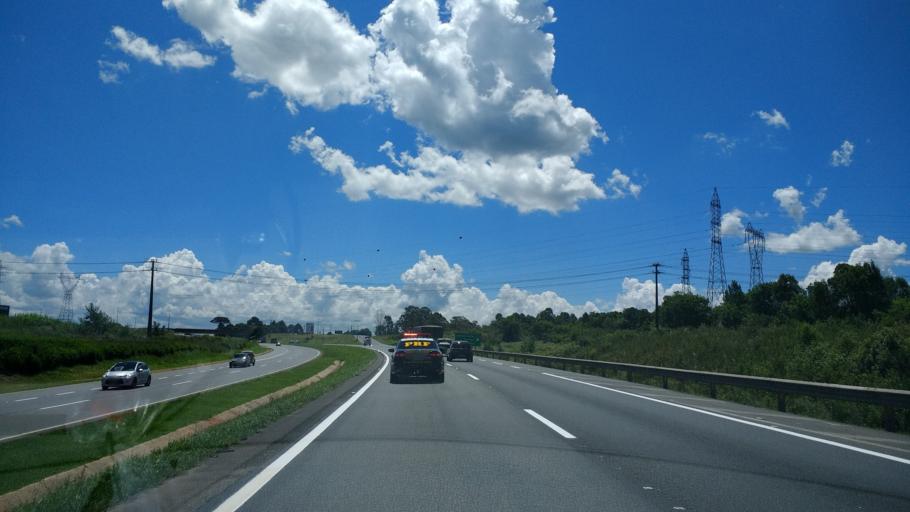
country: BR
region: Parana
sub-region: Campo Largo
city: Campo Largo
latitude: -25.4369
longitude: -49.5144
